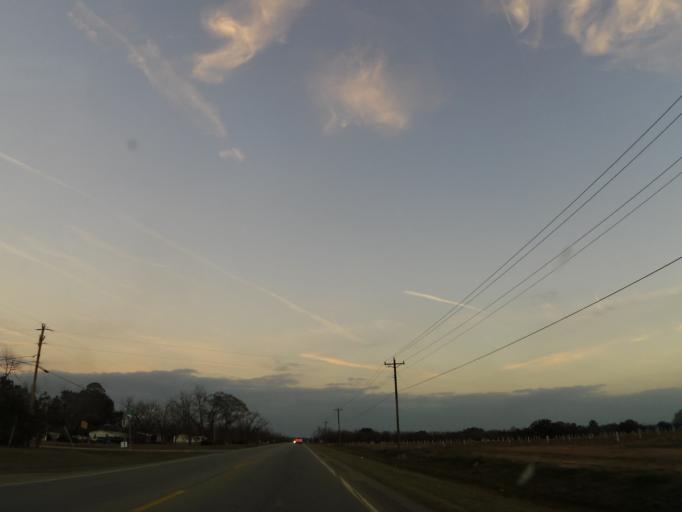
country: US
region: Georgia
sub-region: Dougherty County
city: Putney
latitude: 31.5317
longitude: -84.0919
